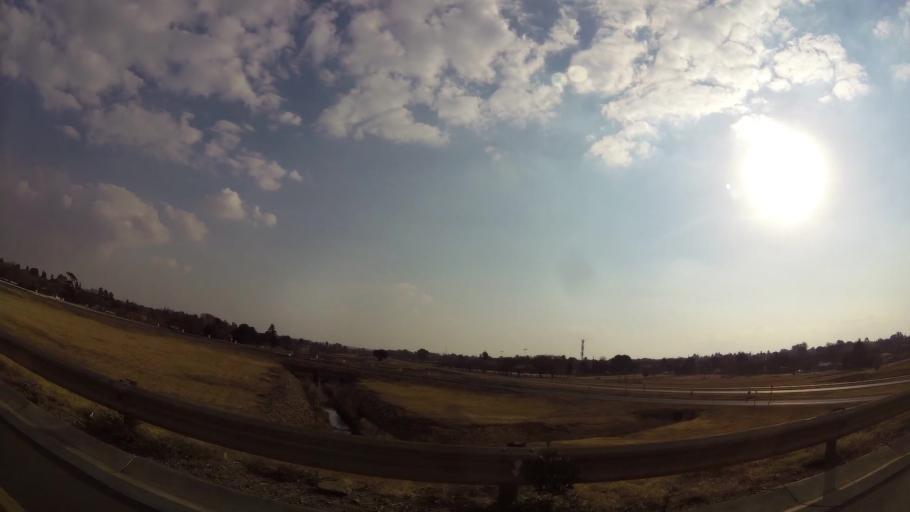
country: ZA
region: Gauteng
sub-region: Ekurhuleni Metropolitan Municipality
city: Springs
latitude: -26.2806
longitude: 28.4530
